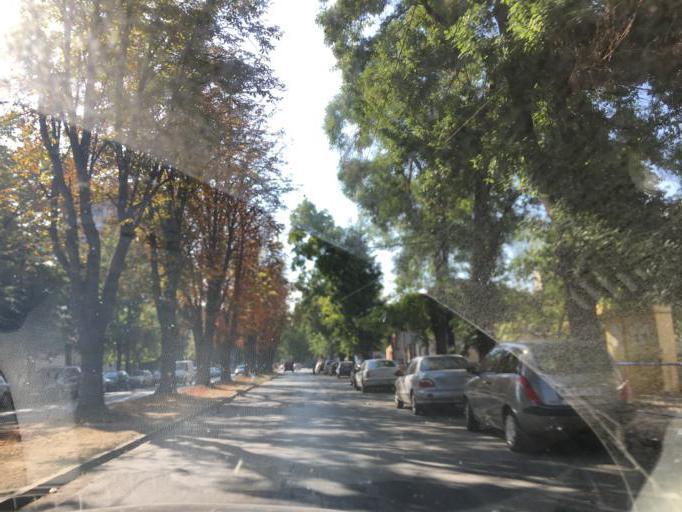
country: BG
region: Pazardzhik
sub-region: Obshtina Pazardzhik
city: Pazardzhik
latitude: 42.2009
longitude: 24.3324
